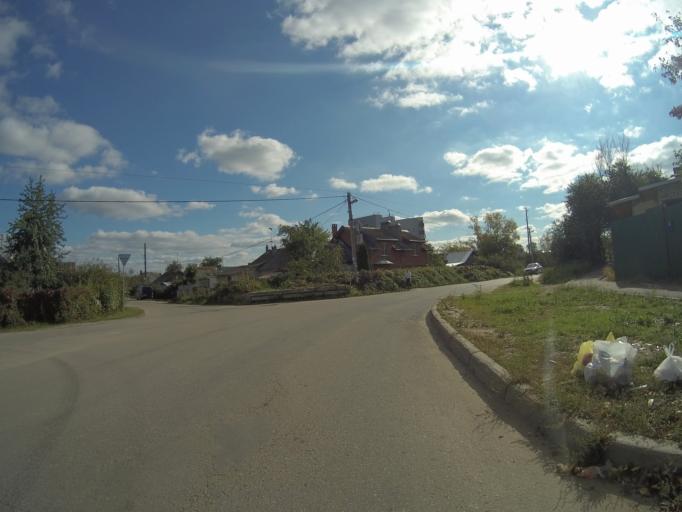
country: RU
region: Vladimir
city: Vladimir
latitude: 56.1131
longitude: 40.3661
